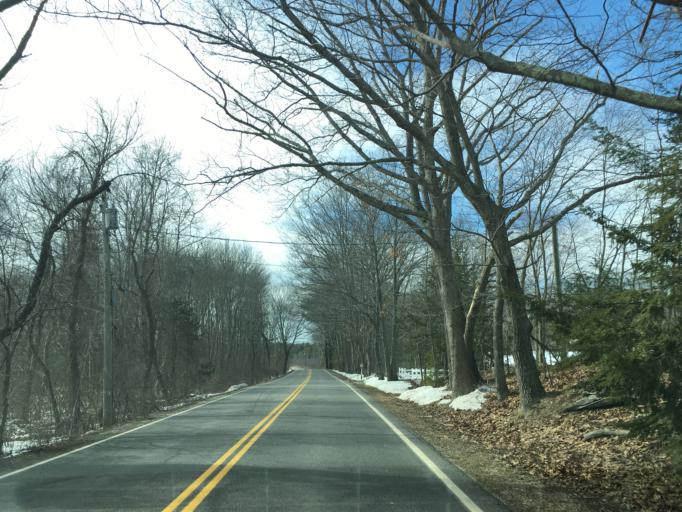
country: US
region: New Hampshire
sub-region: Rockingham County
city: North Hampton
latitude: 42.9957
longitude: -70.8556
